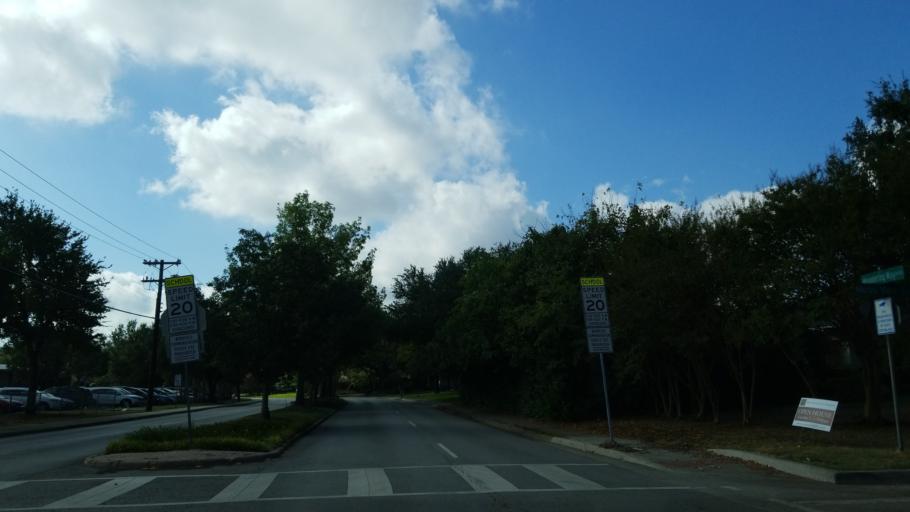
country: US
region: Texas
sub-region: Dallas County
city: Richardson
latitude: 32.9476
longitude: -96.7787
